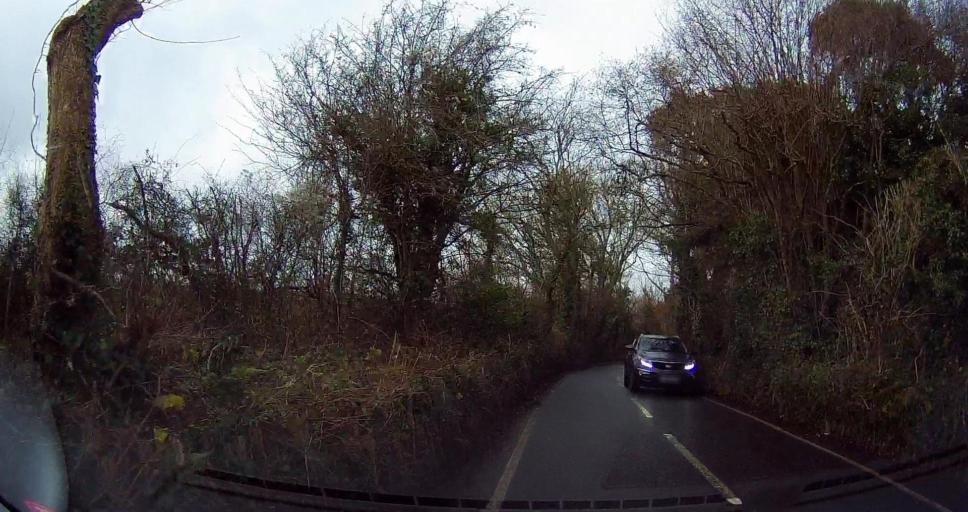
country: GB
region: England
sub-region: Kent
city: Biggin Hill
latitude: 51.3190
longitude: 0.0722
